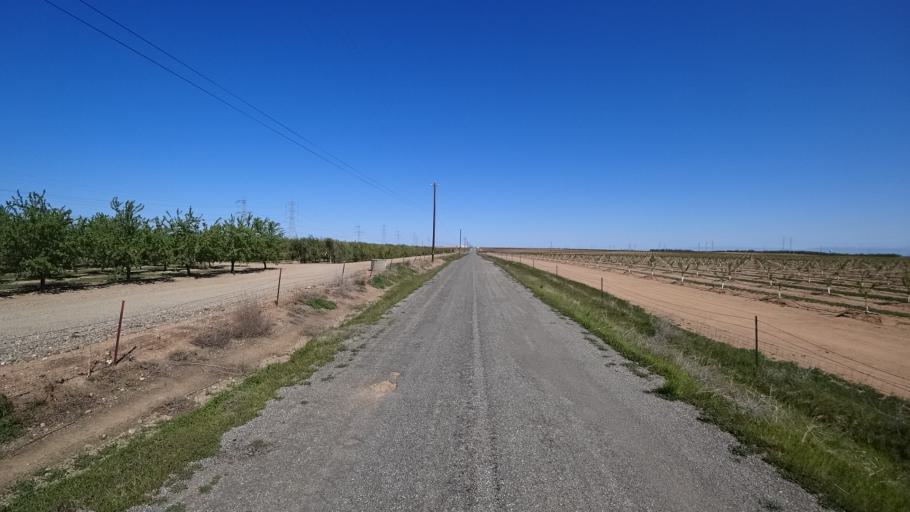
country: US
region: California
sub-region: Glenn County
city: Orland
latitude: 39.6653
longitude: -122.2719
